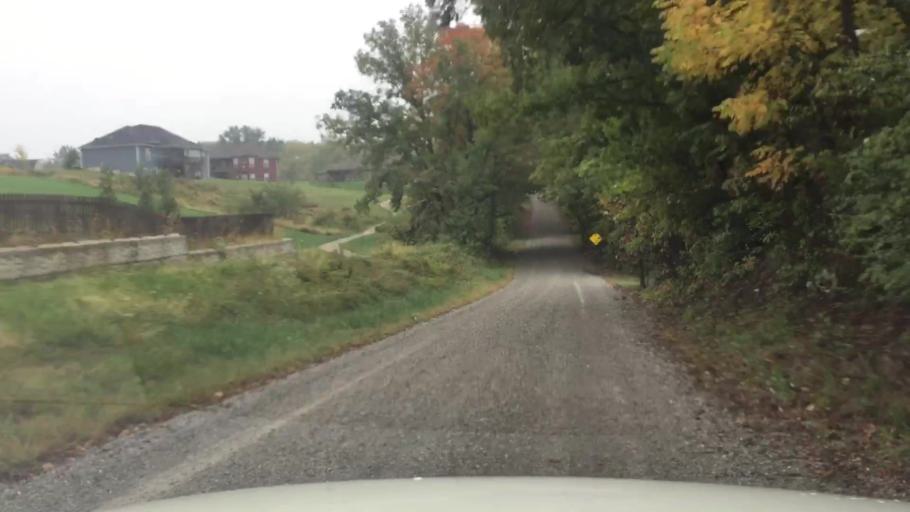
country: US
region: Missouri
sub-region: Boone County
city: Columbia
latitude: 38.8888
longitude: -92.4196
